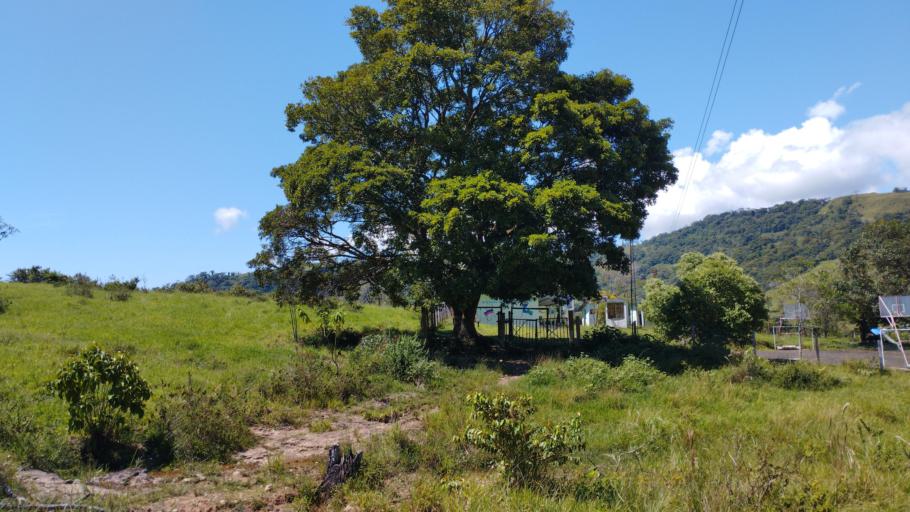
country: CO
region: Boyaca
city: San Luis de Gaceno
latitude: 4.7927
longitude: -73.1095
